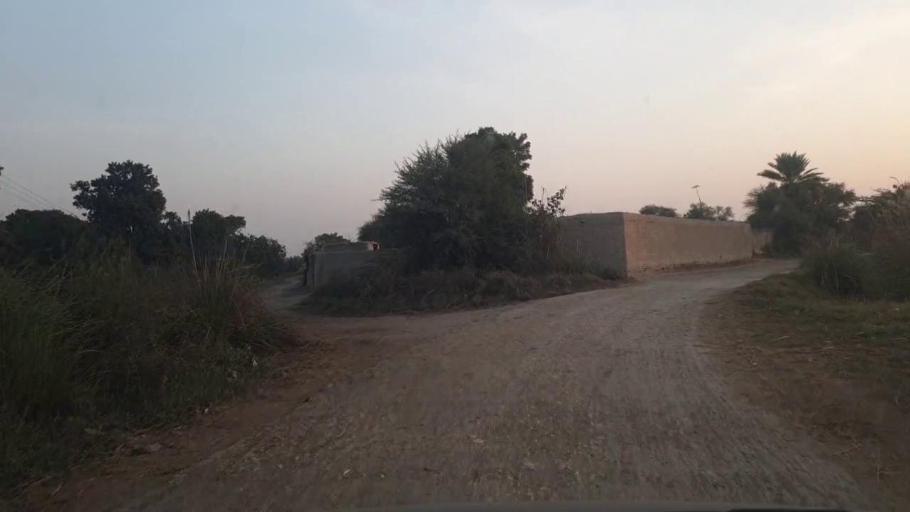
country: PK
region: Sindh
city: Bhit Shah
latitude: 25.8633
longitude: 68.5180
